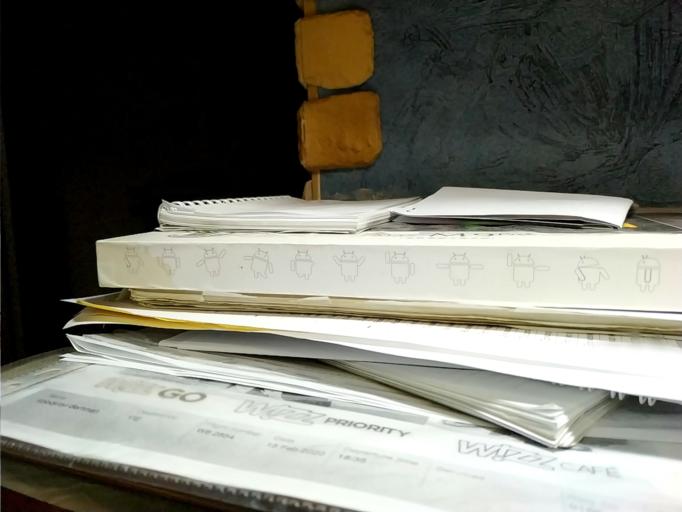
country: RU
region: Arkhangelskaya
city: Onega
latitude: 63.3808
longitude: 38.2158
